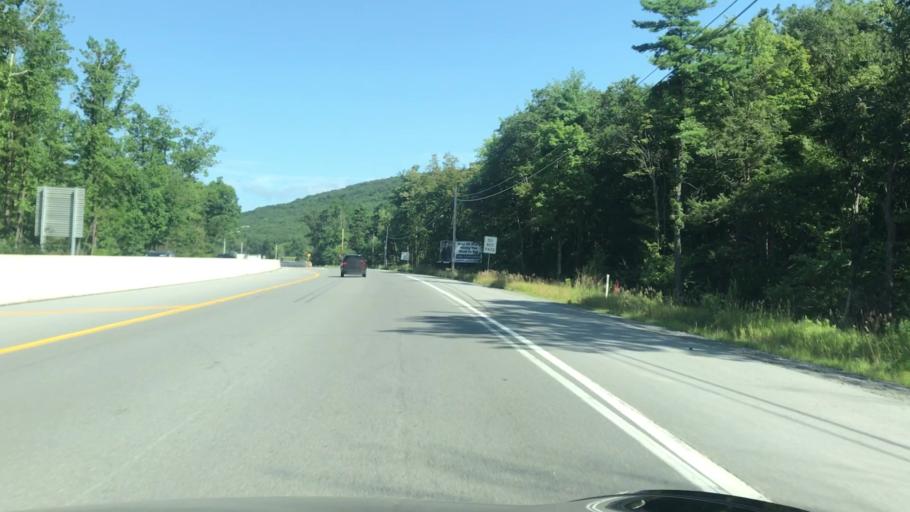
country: US
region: Pennsylvania
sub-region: Lycoming County
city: Montoursville
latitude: 41.2095
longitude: -76.9213
